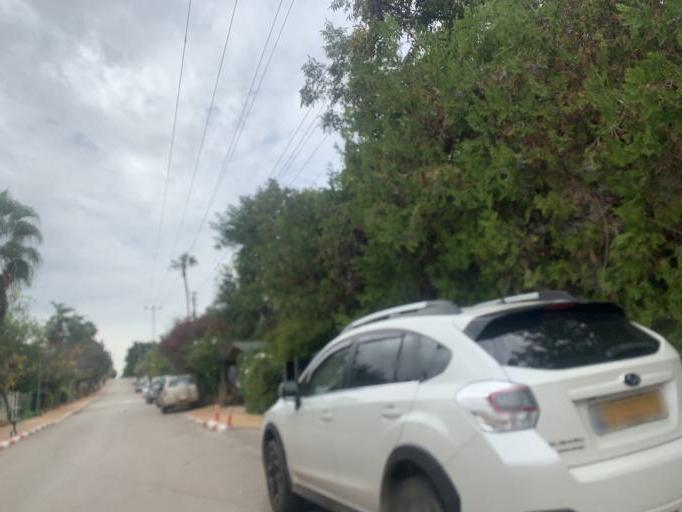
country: IL
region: Central District
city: Hod HaSharon
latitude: 32.1658
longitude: 34.8860
